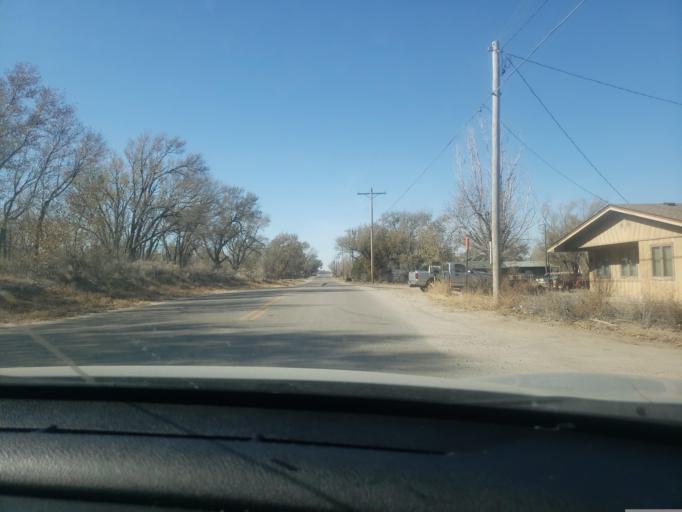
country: US
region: Kansas
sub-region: Finney County
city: Garden City
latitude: 37.9512
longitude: -100.8731
